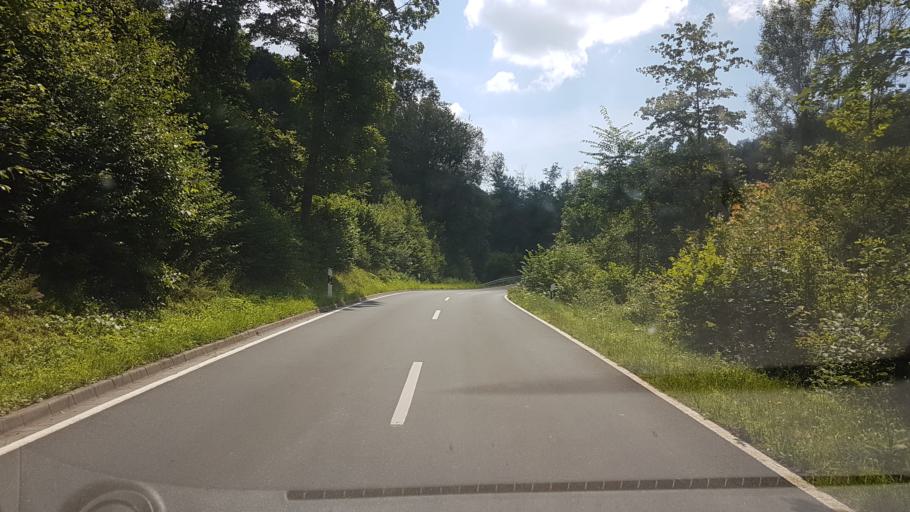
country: DE
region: Bavaria
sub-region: Upper Franconia
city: Egloffstein
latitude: 49.7253
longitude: 11.2285
